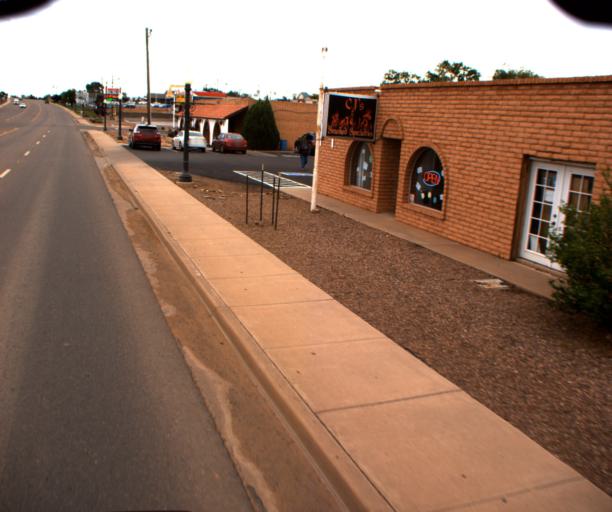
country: US
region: Arizona
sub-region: Navajo County
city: Snowflake
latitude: 34.5006
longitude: -110.0792
